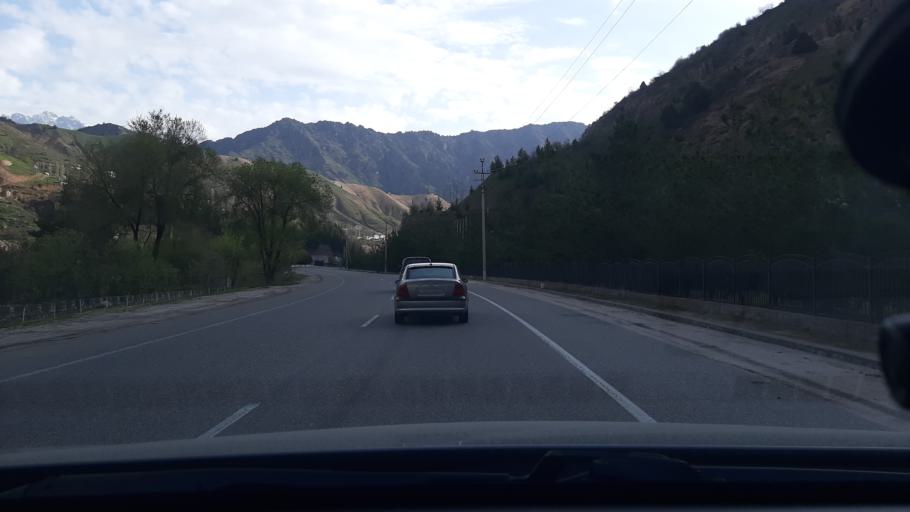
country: TJ
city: Varzob
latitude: 38.8382
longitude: 68.8282
